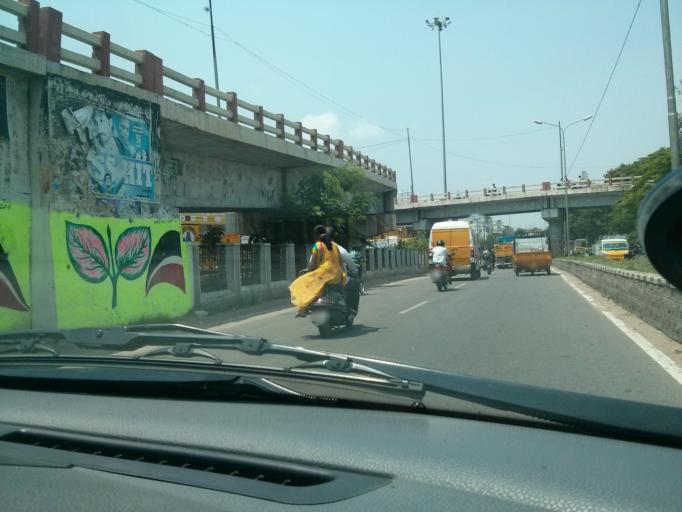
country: IN
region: Tamil Nadu
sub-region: Coimbatore
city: Coimbatore
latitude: 11.0173
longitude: 76.9539
